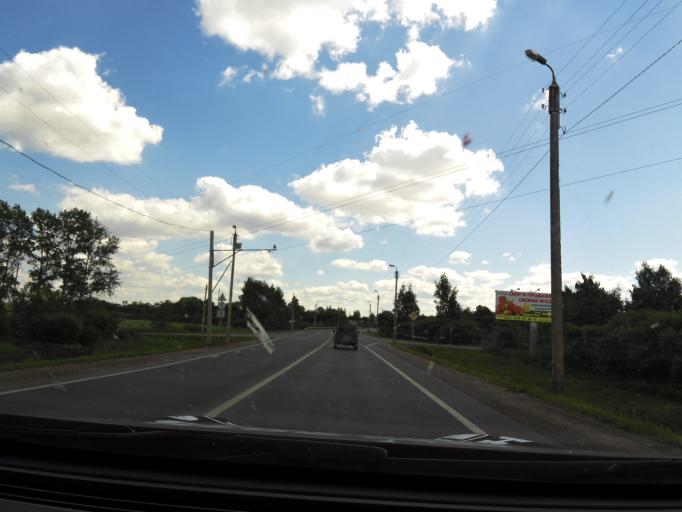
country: RU
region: Vologda
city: Vologda
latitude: 59.2423
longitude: 39.7868
